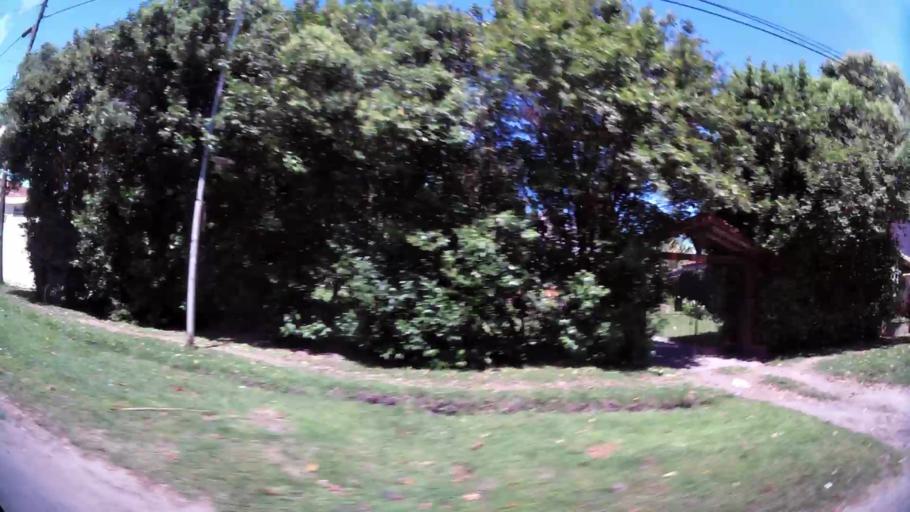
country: AR
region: Buenos Aires
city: Hurlingham
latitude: -34.4997
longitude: -58.6379
